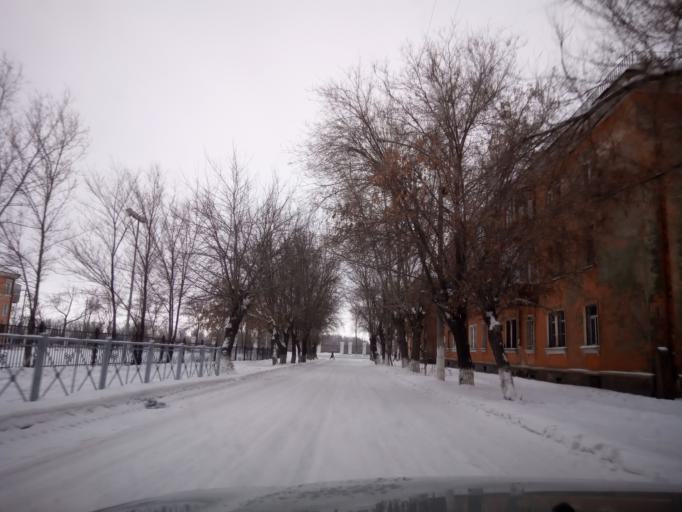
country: RU
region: Orenburg
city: Novotroitsk
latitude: 51.1966
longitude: 58.3269
